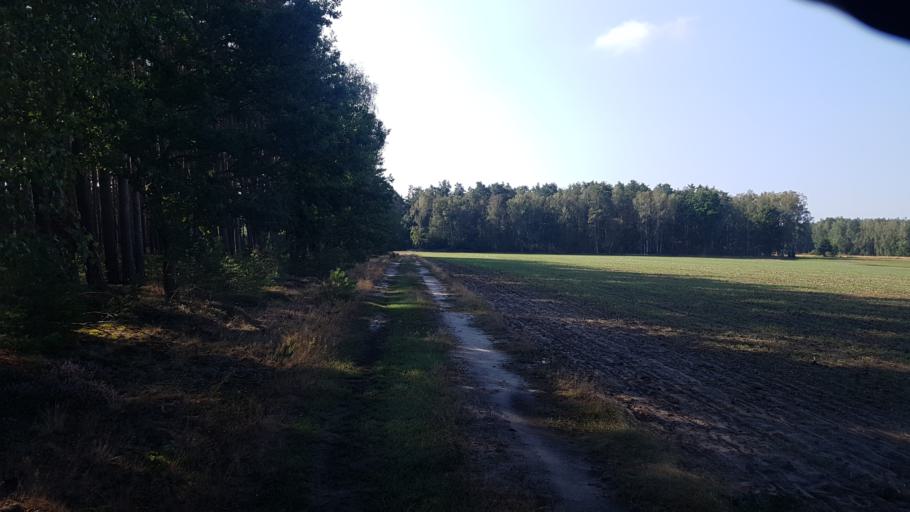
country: DE
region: Brandenburg
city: Finsterwalde
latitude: 51.5950
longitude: 13.6784
